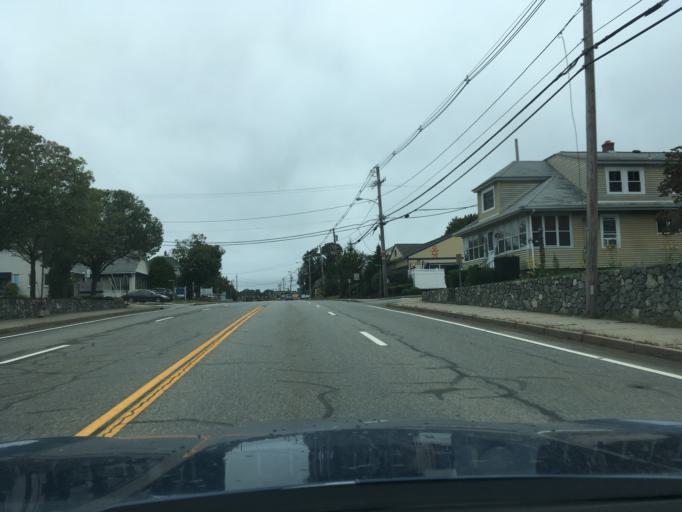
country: US
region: Rhode Island
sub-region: Kent County
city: East Greenwich
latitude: 41.6518
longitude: -71.4565
